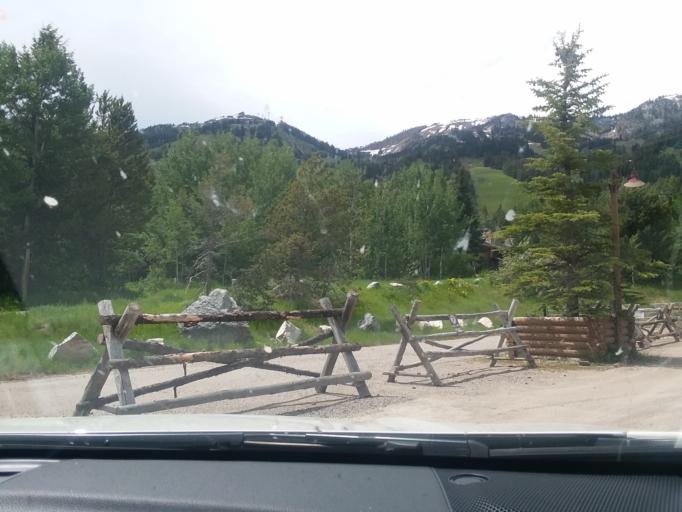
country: US
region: Wyoming
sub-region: Teton County
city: Moose Wilson Road
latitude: 43.5866
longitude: -110.8310
